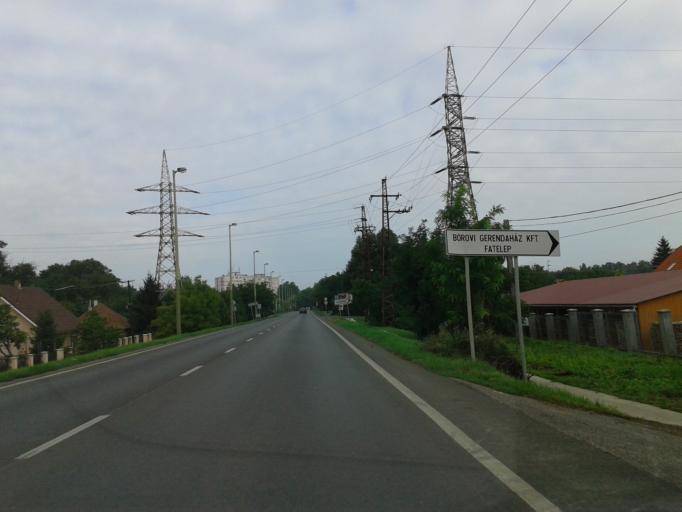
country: HU
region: Csongrad
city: Szeged
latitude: 46.2400
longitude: 20.1661
